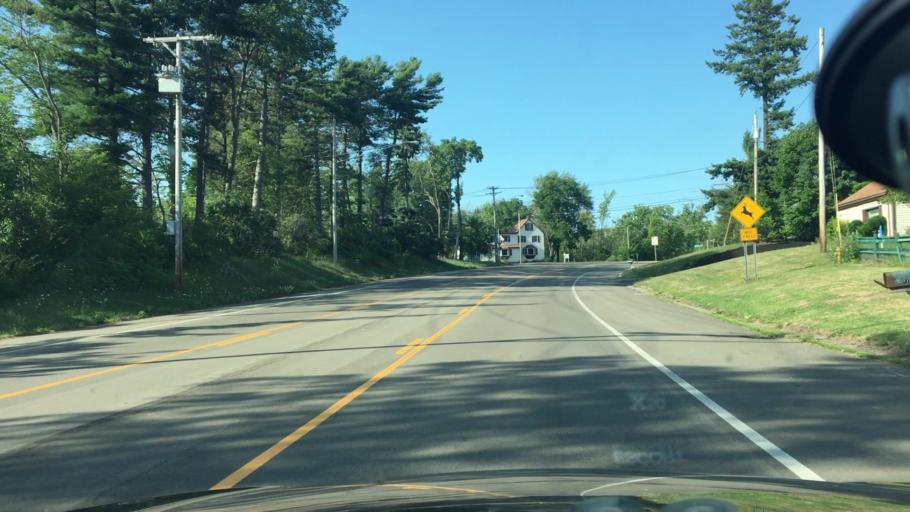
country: US
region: New York
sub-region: Erie County
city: Eden
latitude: 42.6969
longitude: -78.9355
